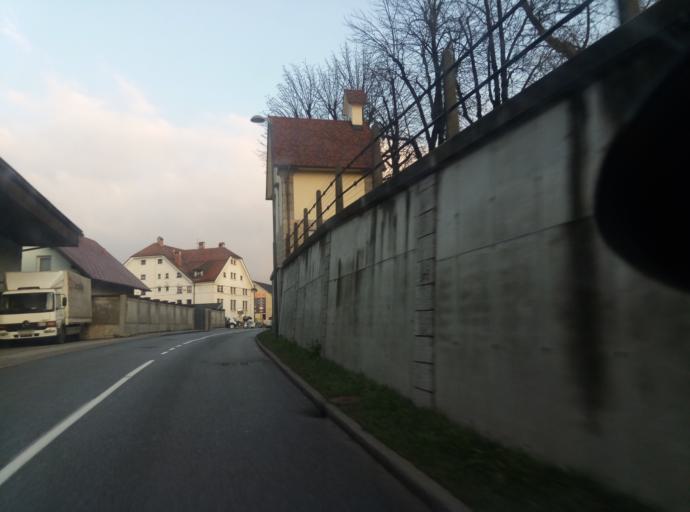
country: SI
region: Kranj
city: Kranj
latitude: 46.2367
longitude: 14.3538
